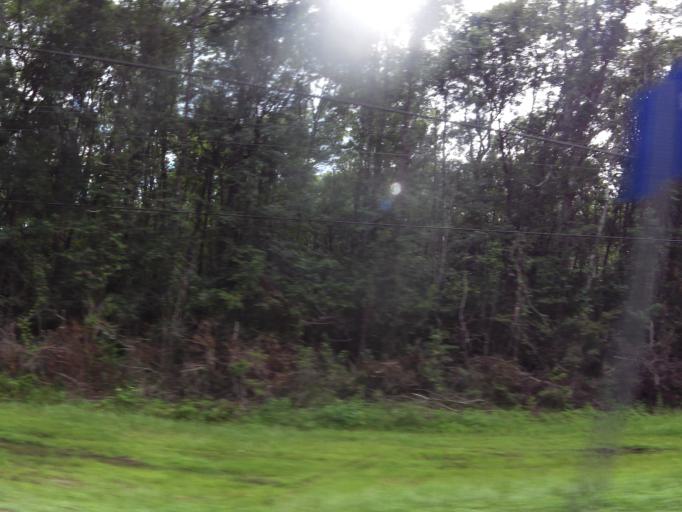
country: US
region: Florida
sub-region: Clay County
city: Asbury Lake
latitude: 30.0740
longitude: -81.7769
